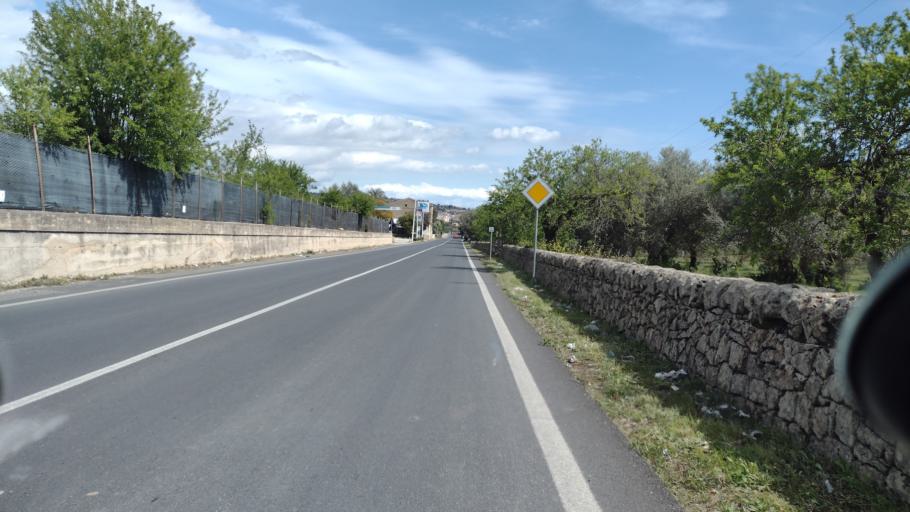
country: IT
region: Sicily
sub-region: Provincia di Siracusa
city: Noto
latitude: 36.8768
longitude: 15.0526
